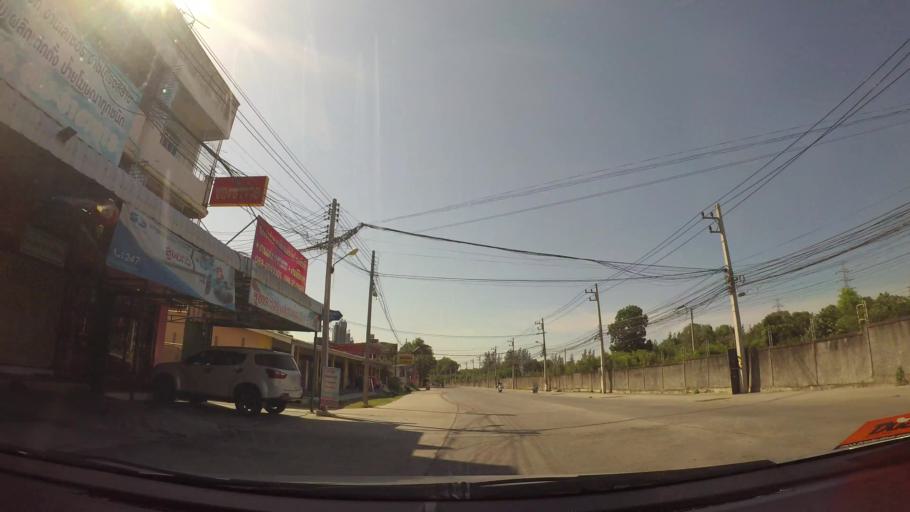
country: TH
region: Chon Buri
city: Si Racha
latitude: 13.1578
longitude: 100.9411
